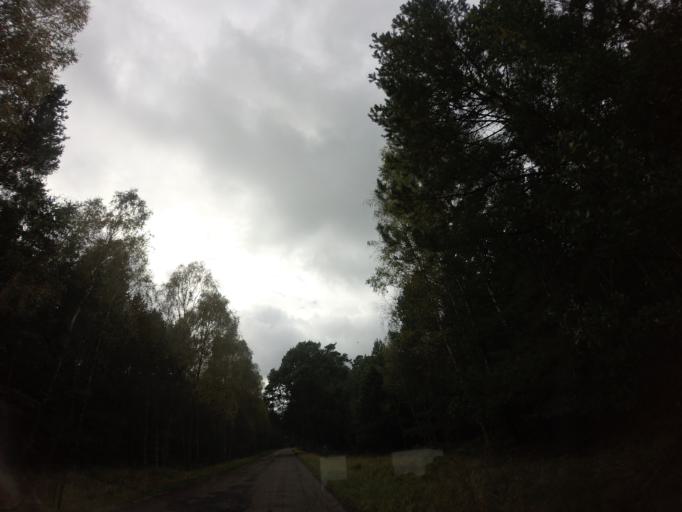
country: PL
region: West Pomeranian Voivodeship
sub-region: Powiat goleniowski
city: Przybiernow
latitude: 53.7061
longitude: 14.7319
